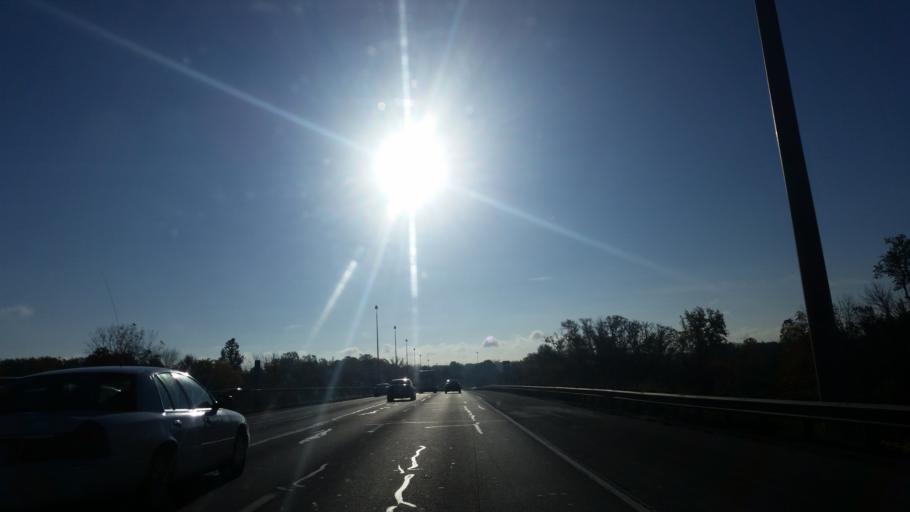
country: US
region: Ohio
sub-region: Summit County
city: Fairlawn
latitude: 41.1050
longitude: -81.5963
